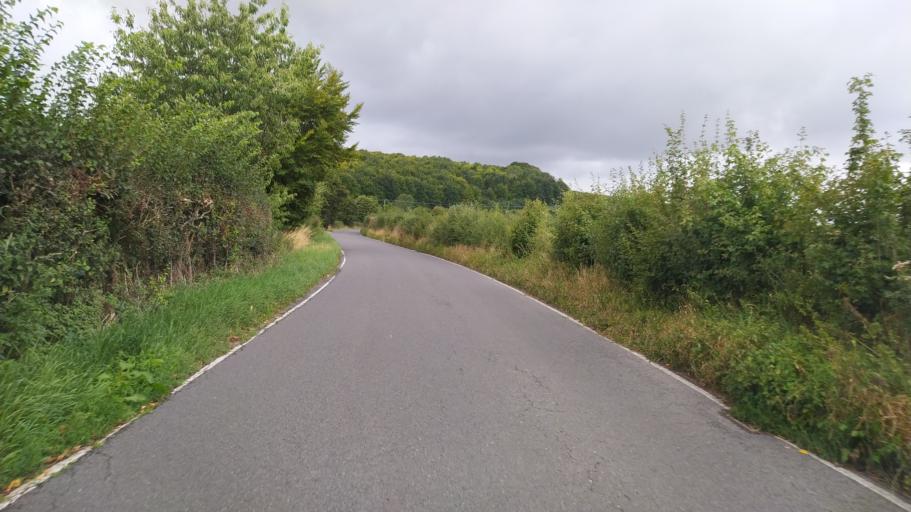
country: GB
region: England
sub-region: Hampshire
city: Cowplain
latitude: 50.9966
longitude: -1.0385
